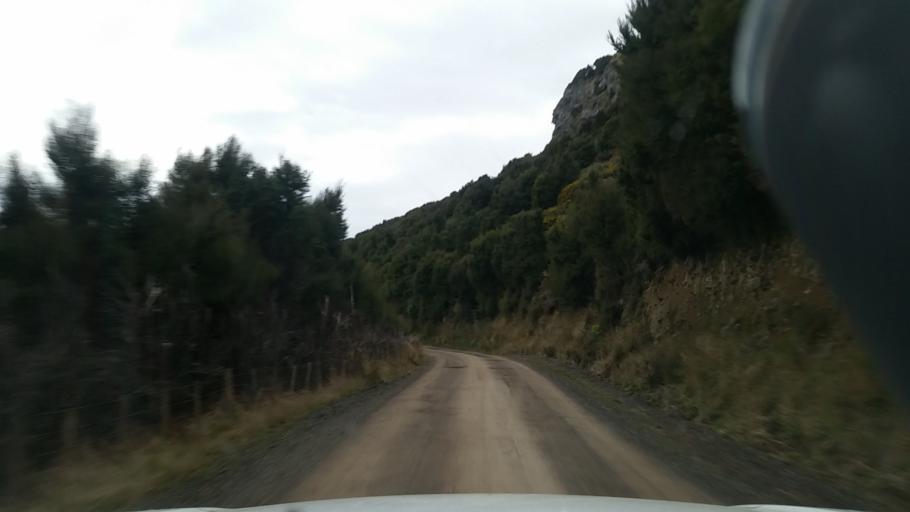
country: NZ
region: Canterbury
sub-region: Christchurch City
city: Christchurch
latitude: -43.8446
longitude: 172.9715
